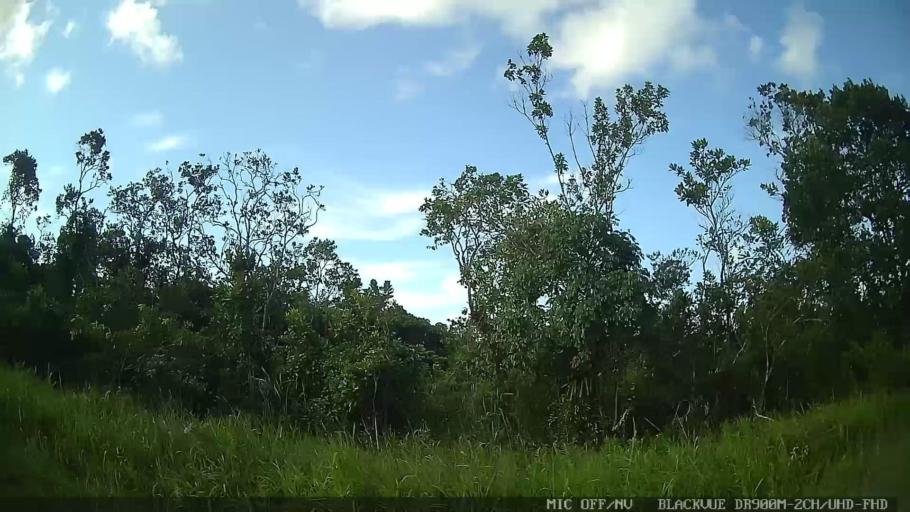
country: BR
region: Sao Paulo
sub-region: Itanhaem
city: Itanhaem
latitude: -24.1728
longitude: -46.8381
